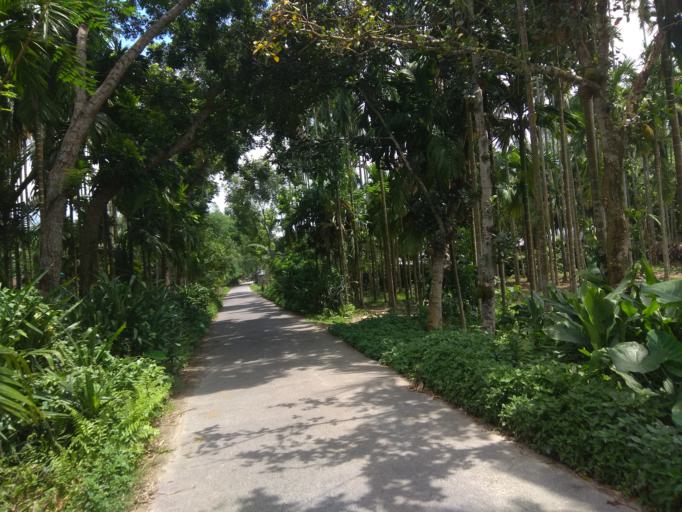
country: IN
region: West Bengal
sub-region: Koch Bihar
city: Haldibari
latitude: 26.1628
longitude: 88.9242
